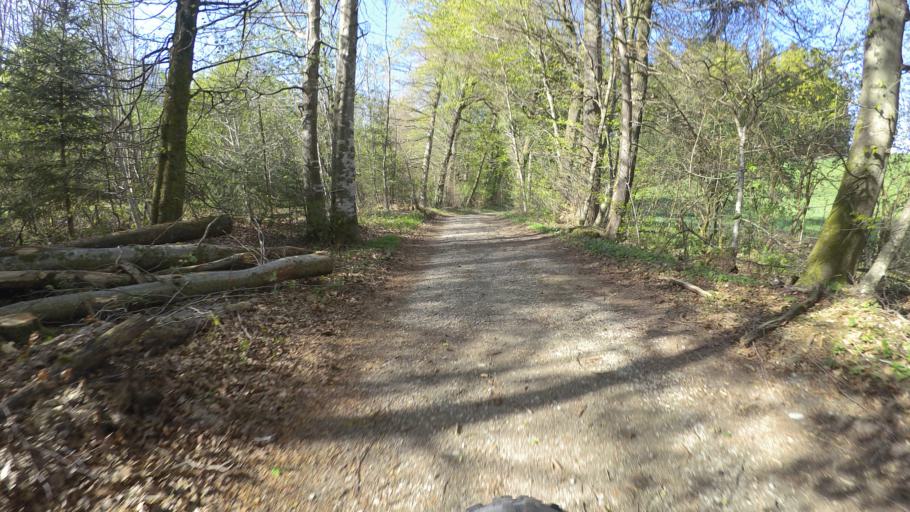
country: DE
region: Bavaria
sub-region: Upper Bavaria
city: Grabenstatt
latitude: 47.8602
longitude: 12.5681
